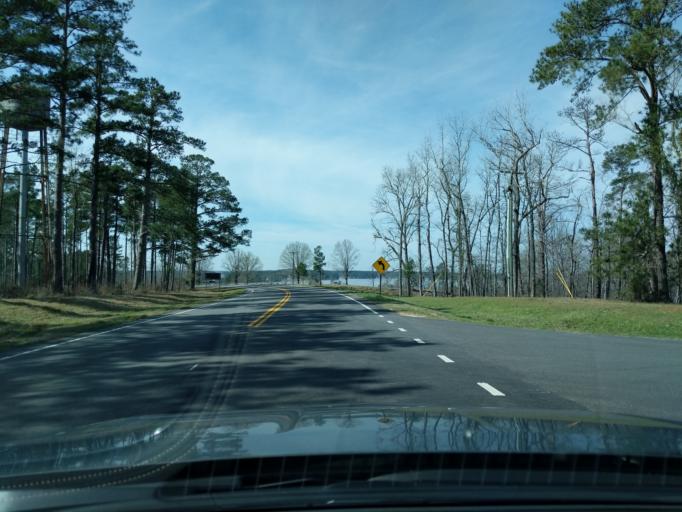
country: US
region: Georgia
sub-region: Columbia County
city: Evans
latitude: 33.6700
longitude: -82.1854
